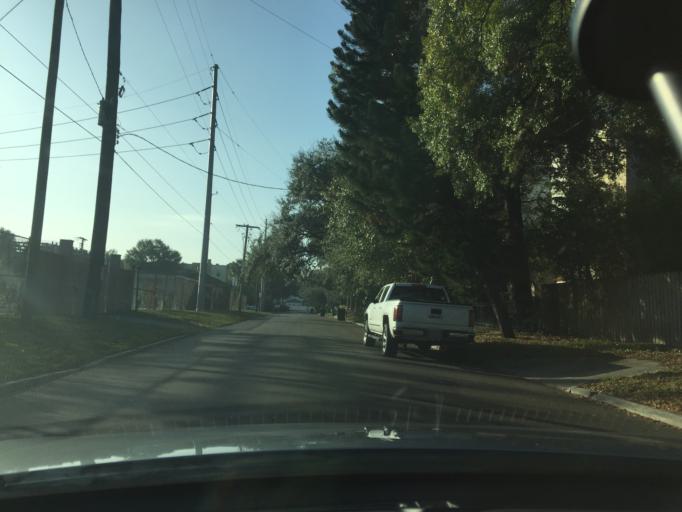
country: US
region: Florida
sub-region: Hillsborough County
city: Tampa
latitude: 27.9397
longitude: -82.4954
